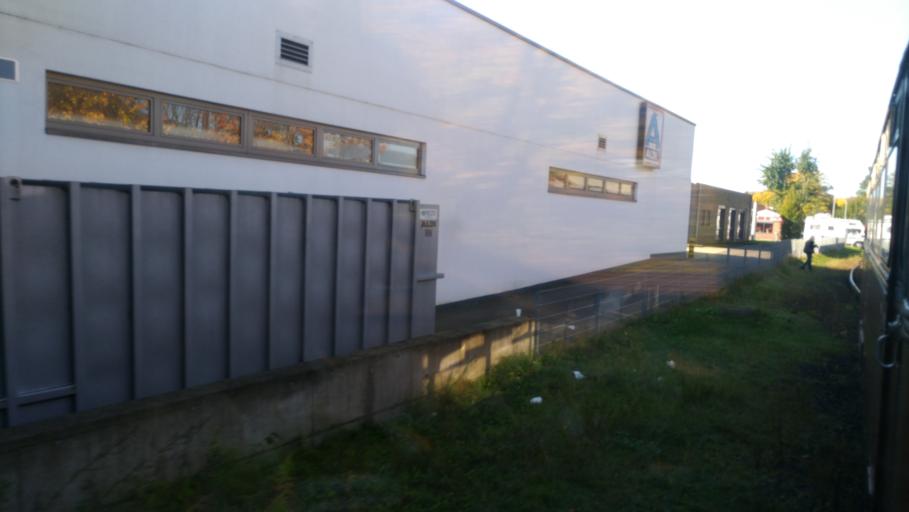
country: DE
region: Lower Saxony
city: Rinteln
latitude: 52.1984
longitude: 9.0818
